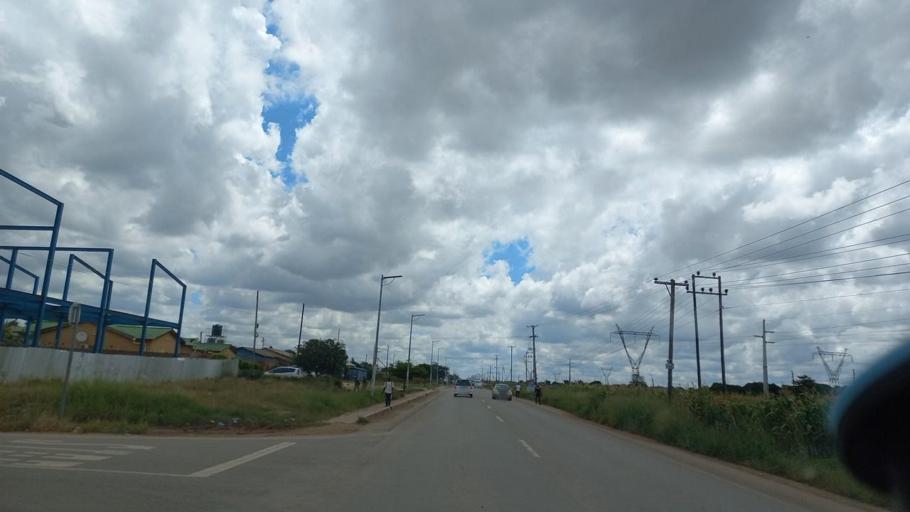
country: ZM
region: Lusaka
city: Lusaka
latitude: -15.4604
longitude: 28.3366
